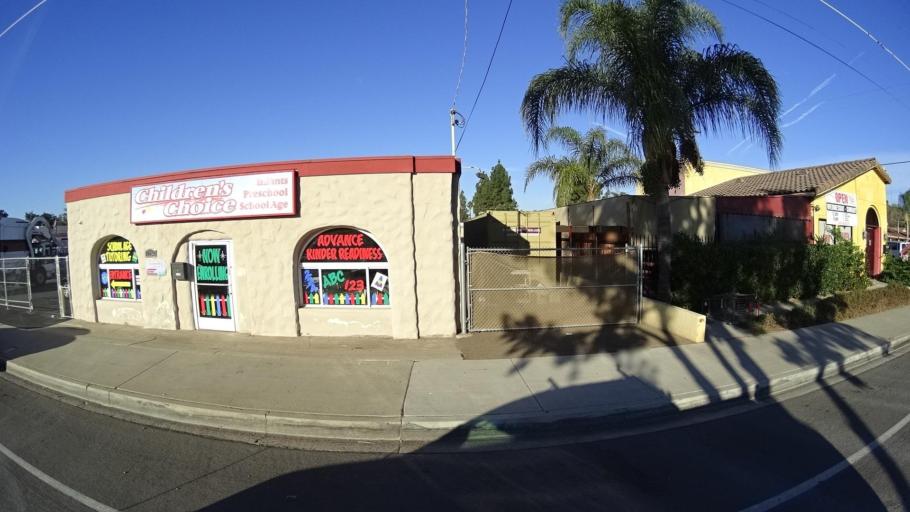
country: US
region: California
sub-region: San Diego County
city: Bostonia
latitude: 32.8114
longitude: -116.9358
